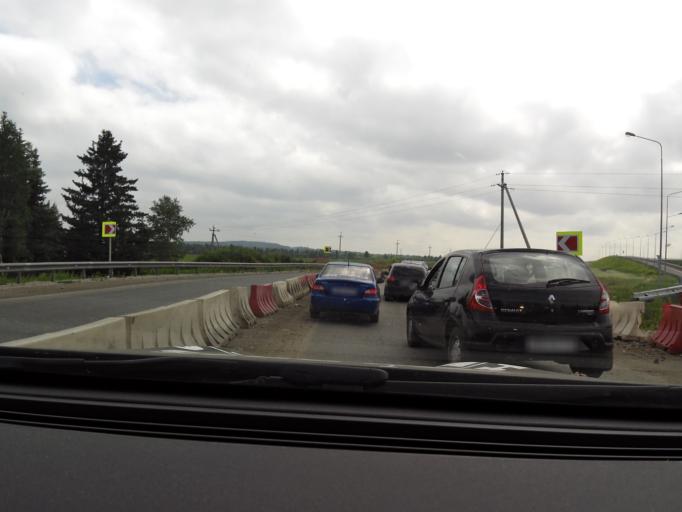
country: RU
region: Perm
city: Zvezdnyy
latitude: 57.7857
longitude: 56.3411
